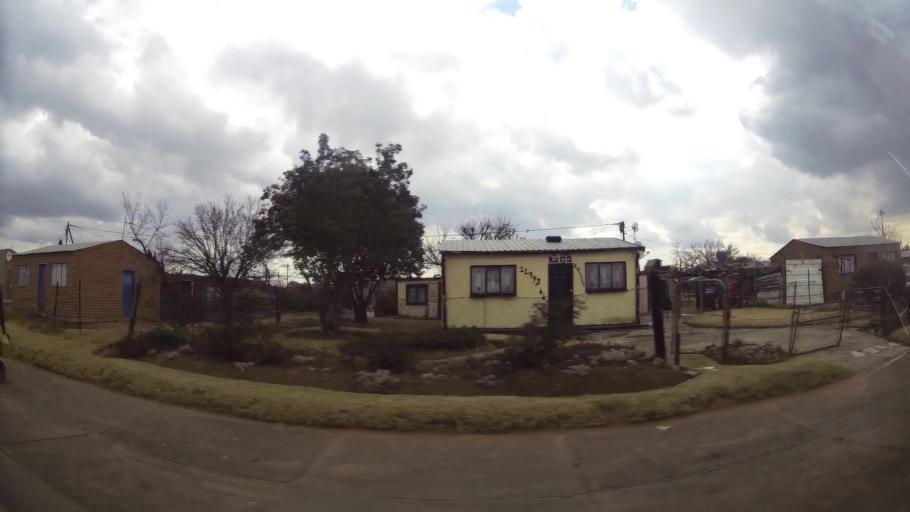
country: ZA
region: Orange Free State
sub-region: Fezile Dabi District Municipality
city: Sasolburg
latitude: -26.8497
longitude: 27.8780
